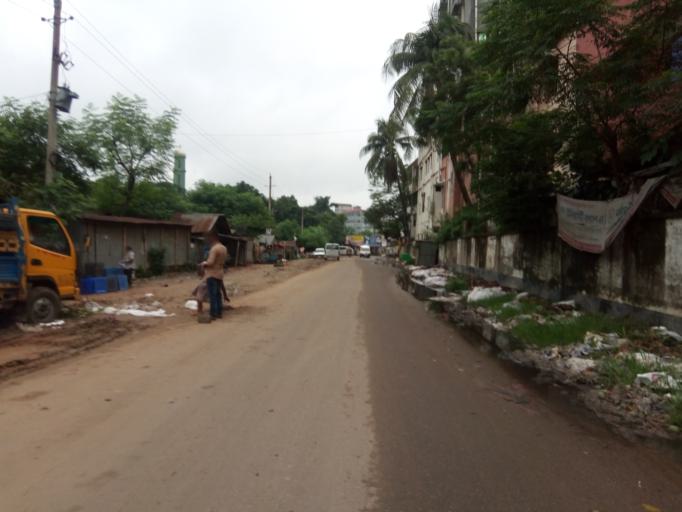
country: BD
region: Dhaka
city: Tungi
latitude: 23.8512
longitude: 90.4133
